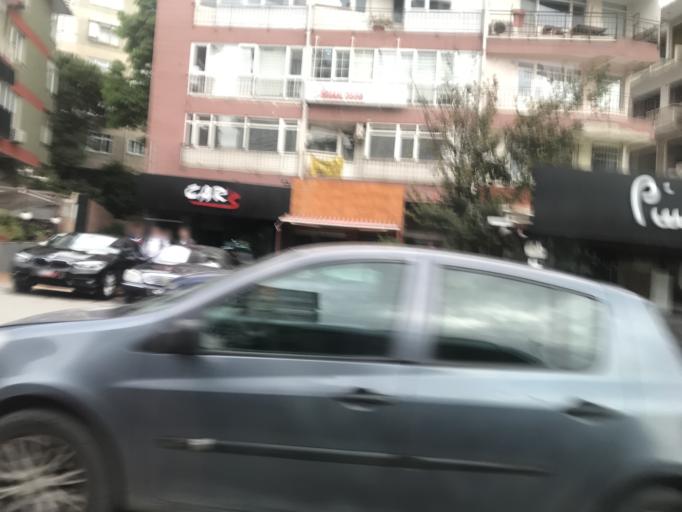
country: TR
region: Istanbul
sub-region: Atasehir
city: Atasehir
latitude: 40.9677
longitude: 29.0860
